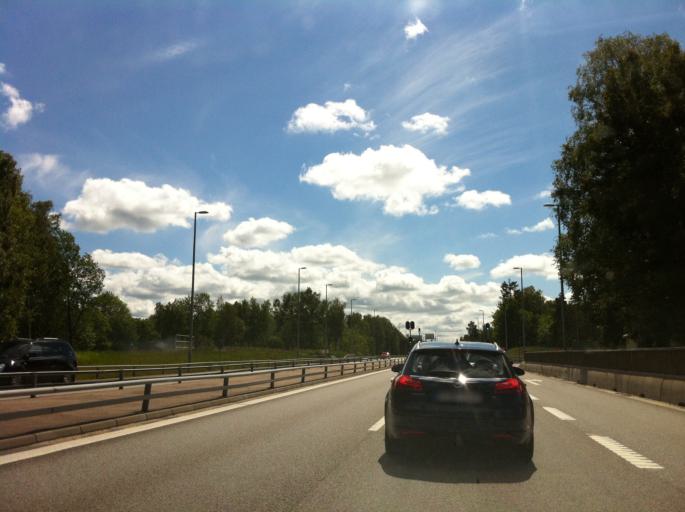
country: SE
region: Vaestra Goetaland
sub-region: Trollhattan
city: Trollhattan
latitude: 58.2798
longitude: 12.3041
